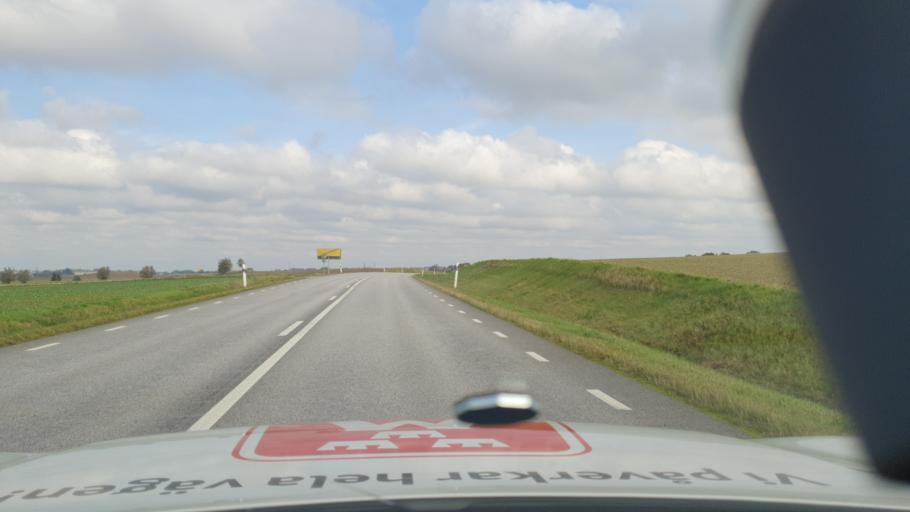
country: SE
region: Skane
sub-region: Trelleborgs Kommun
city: Trelleborg
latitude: 55.4206
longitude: 13.1734
